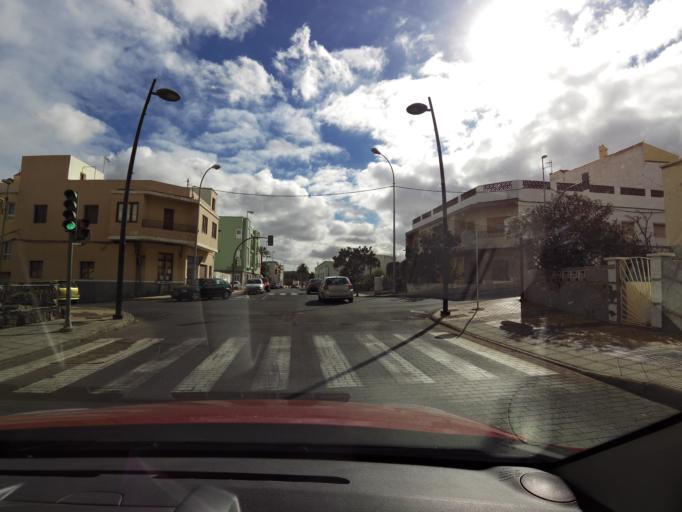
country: ES
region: Canary Islands
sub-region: Provincia de Las Palmas
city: Ingenio
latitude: 27.9183
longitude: -15.4388
